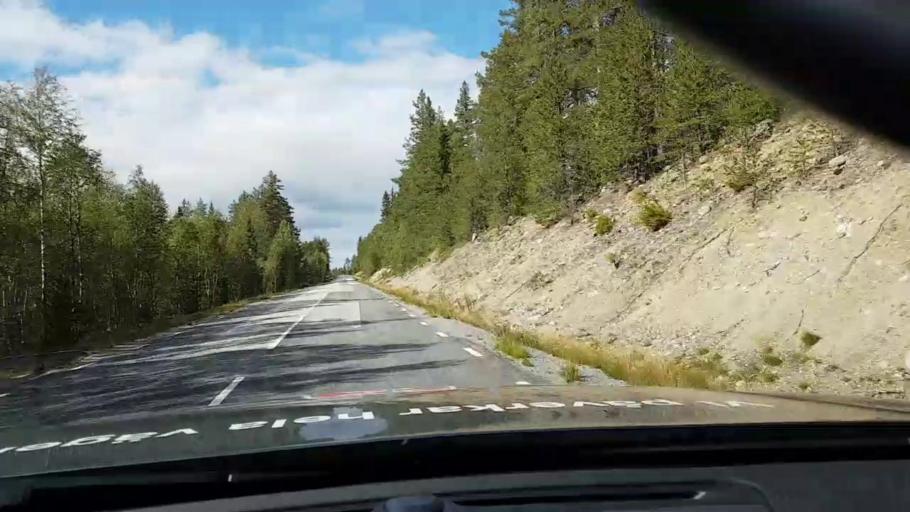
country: SE
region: Vaesterbotten
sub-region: Asele Kommun
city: Asele
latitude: 63.8388
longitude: 17.4329
